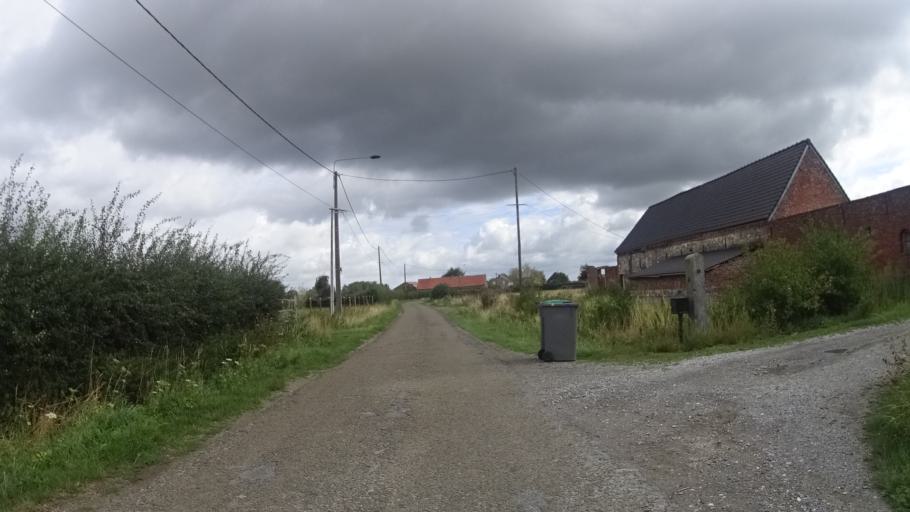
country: FR
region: Nord-Pas-de-Calais
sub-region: Departement du Nord
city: Landrecies
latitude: 50.1216
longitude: 3.7103
